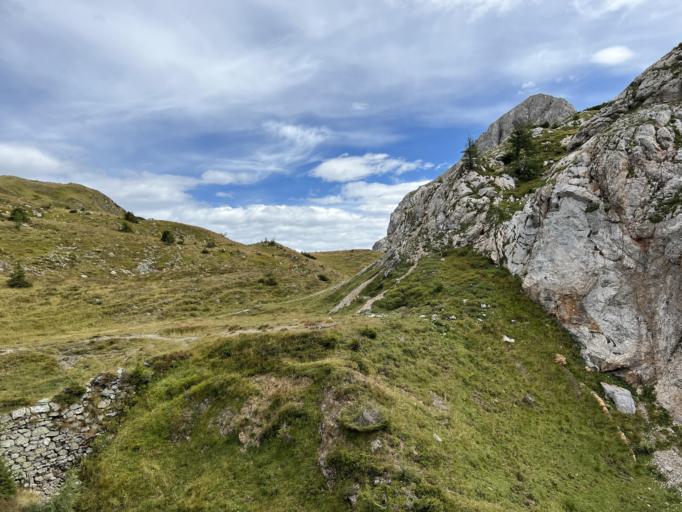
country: IT
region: Friuli Venezia Giulia
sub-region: Provincia di Udine
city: Forni Avoltri
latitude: 46.6267
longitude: 12.8113
